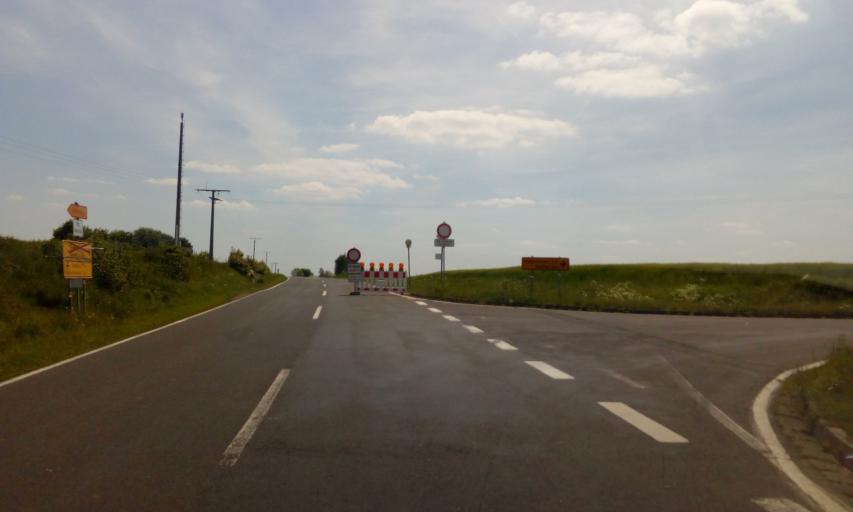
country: DE
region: Rheinland-Pfalz
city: Rodershausen
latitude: 49.9775
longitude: 6.2016
